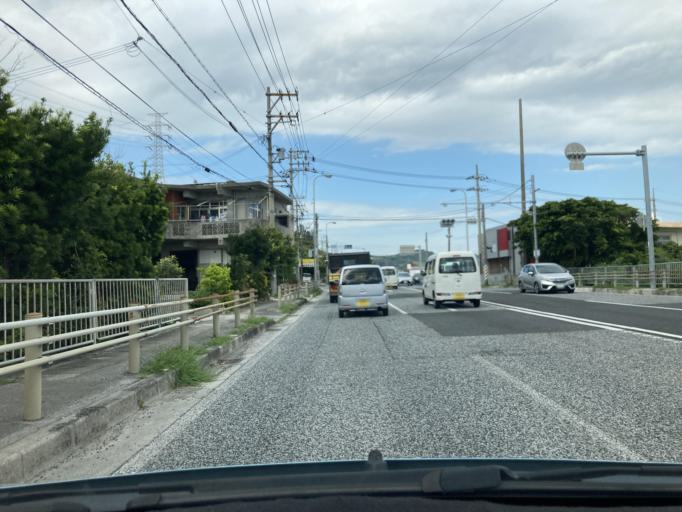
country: JP
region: Okinawa
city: Ginowan
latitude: 26.2547
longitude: 127.7846
